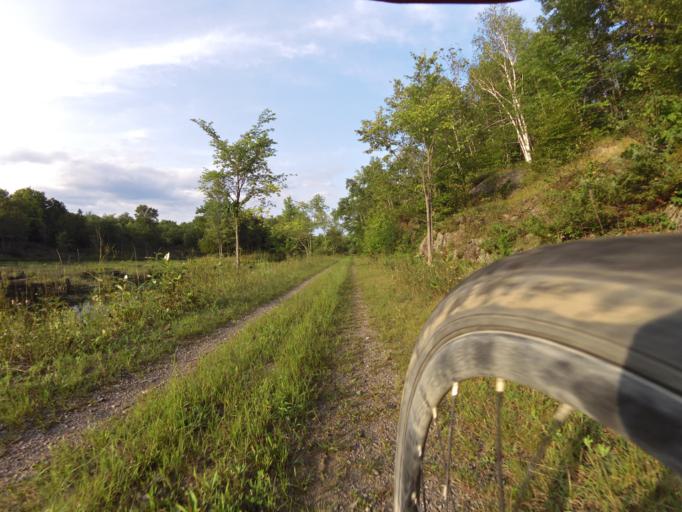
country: CA
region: Ontario
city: Gananoque
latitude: 44.5456
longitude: -76.3947
